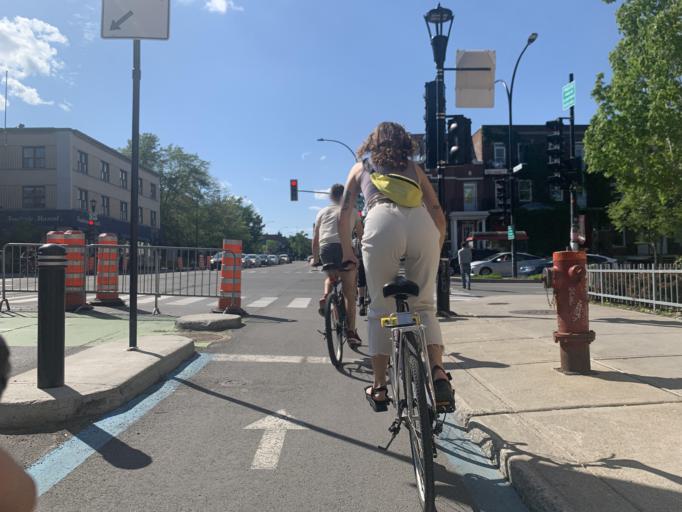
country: CA
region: Quebec
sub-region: Montreal
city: Montreal
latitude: 45.5262
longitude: -73.5876
